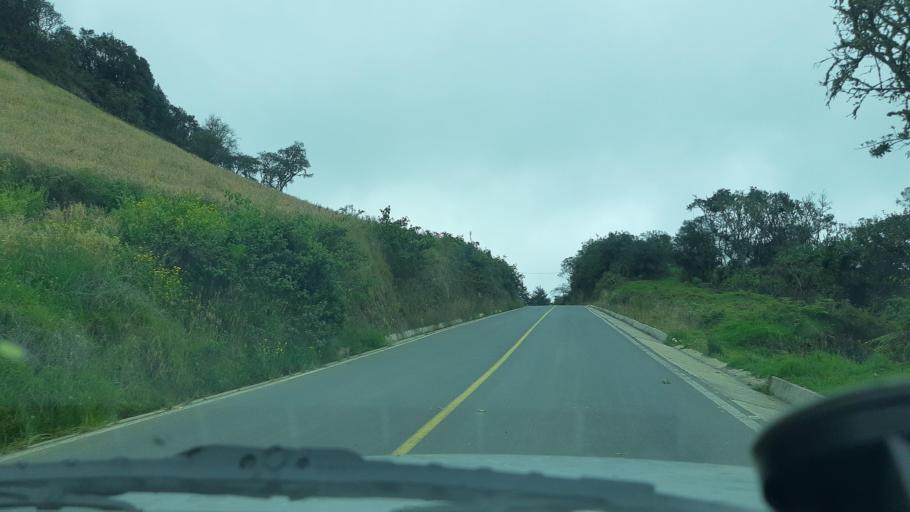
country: CO
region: Cundinamarca
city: Umbita
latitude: 5.2299
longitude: -73.4720
